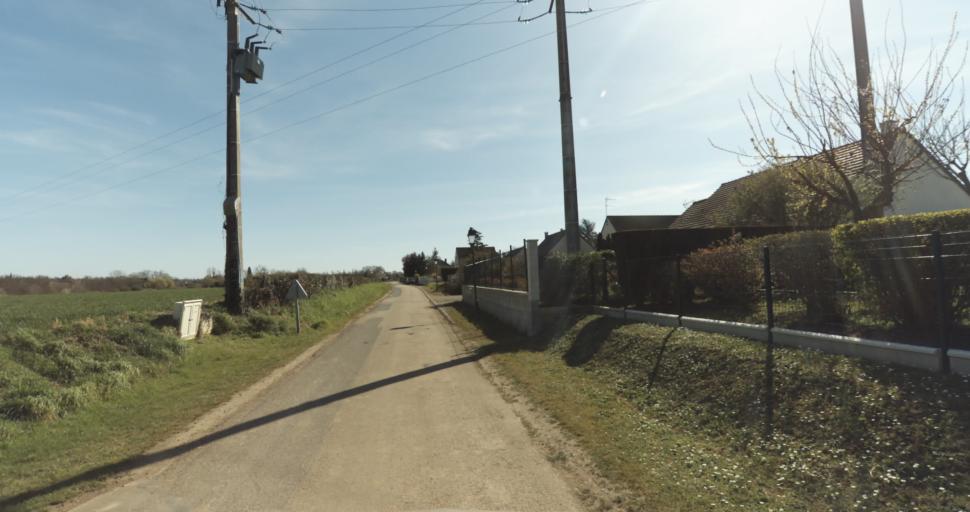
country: FR
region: Lower Normandy
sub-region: Departement du Calvados
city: Saint-Pierre-sur-Dives
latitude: 49.0446
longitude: -0.0265
